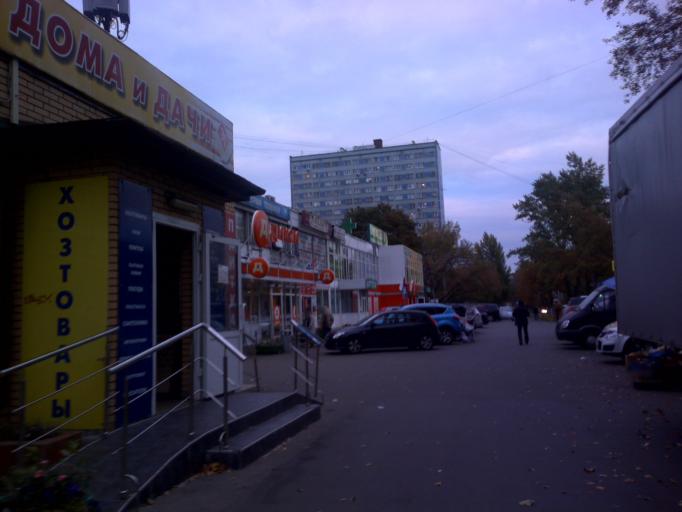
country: RU
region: Moscow
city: Novyye Cheremushki
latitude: 55.6918
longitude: 37.5881
